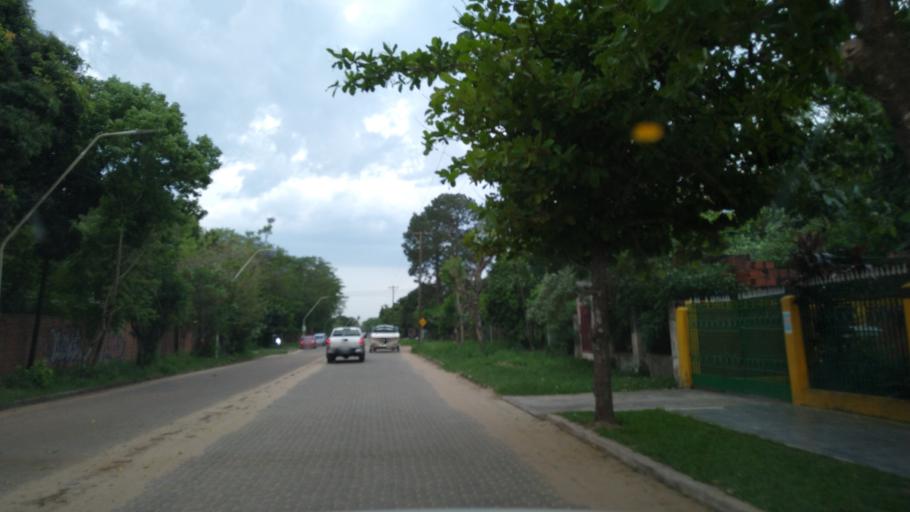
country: AR
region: Corrientes
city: Ituzaingo
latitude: -27.5904
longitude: -56.6995
